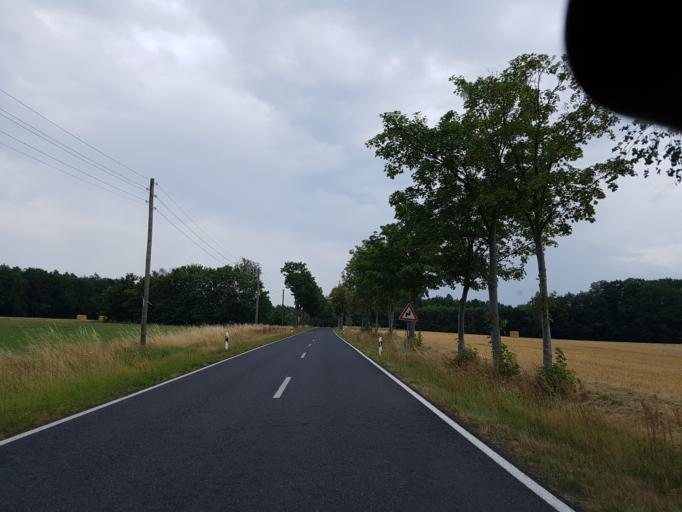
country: DE
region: Brandenburg
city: Sallgast
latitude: 51.5843
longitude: 13.8492
